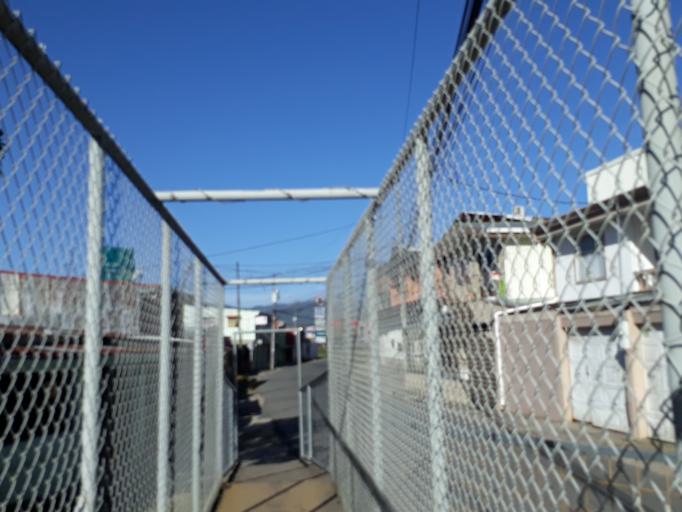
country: CR
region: Cartago
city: Cartago
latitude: 9.8731
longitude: -83.9431
